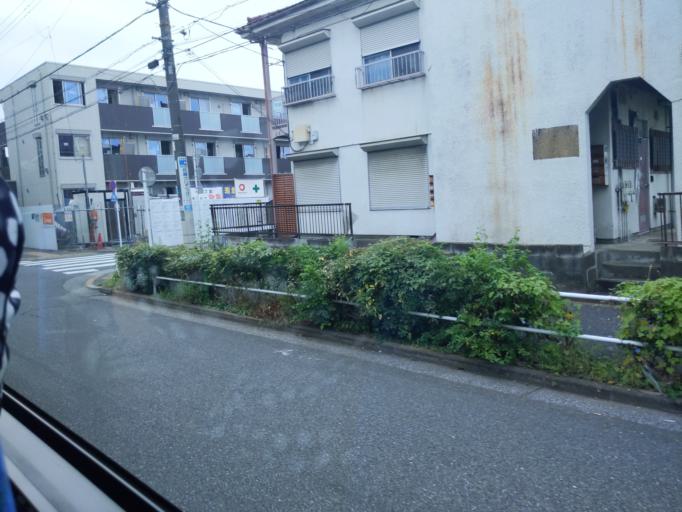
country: JP
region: Saitama
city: Wako
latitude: 35.7876
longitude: 139.6493
